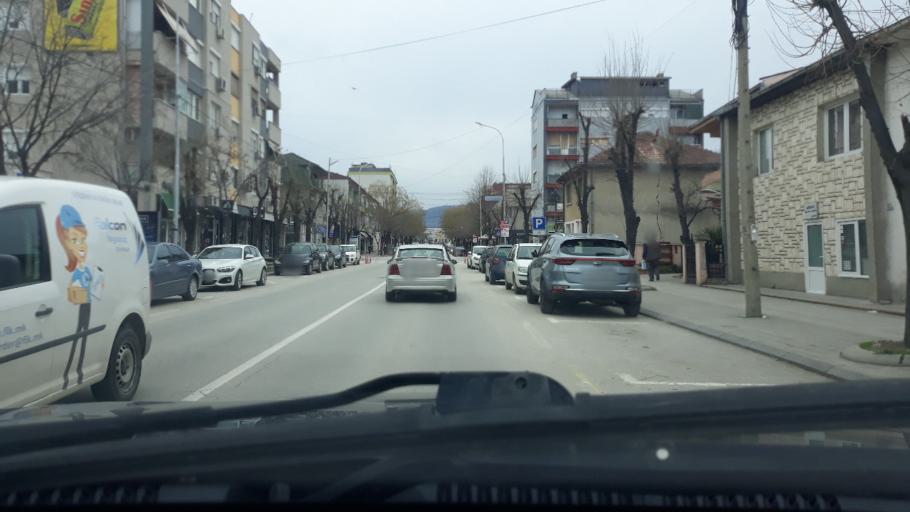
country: MK
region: Kavadarci
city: Kavadarci
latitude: 41.4370
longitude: 22.0108
